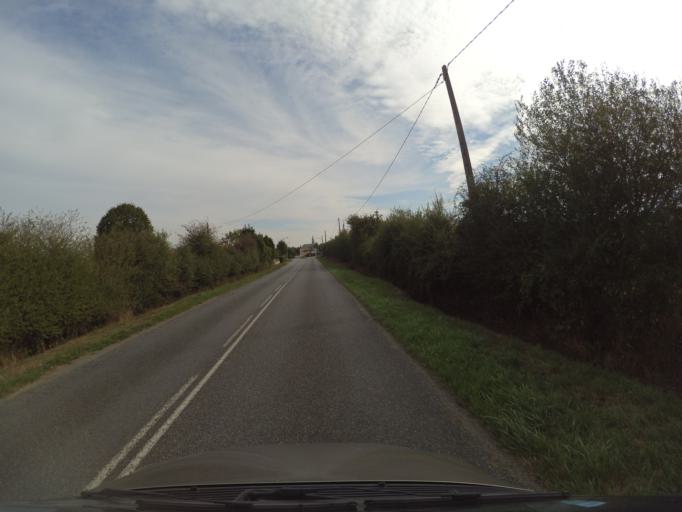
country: FR
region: Pays de la Loire
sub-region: Departement de Maine-et-Loire
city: Chemille-Melay
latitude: 47.2111
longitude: -0.7443
